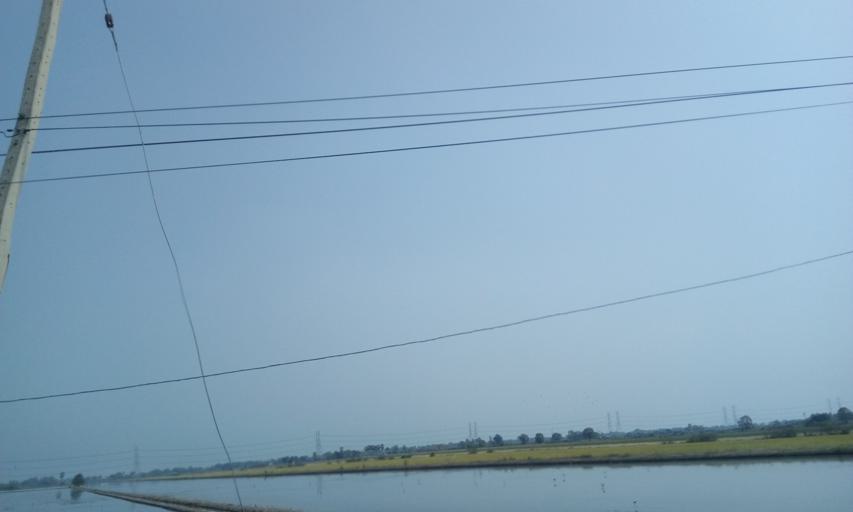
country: TH
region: Pathum Thani
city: Ban Rangsit
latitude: 14.0100
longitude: 100.7578
